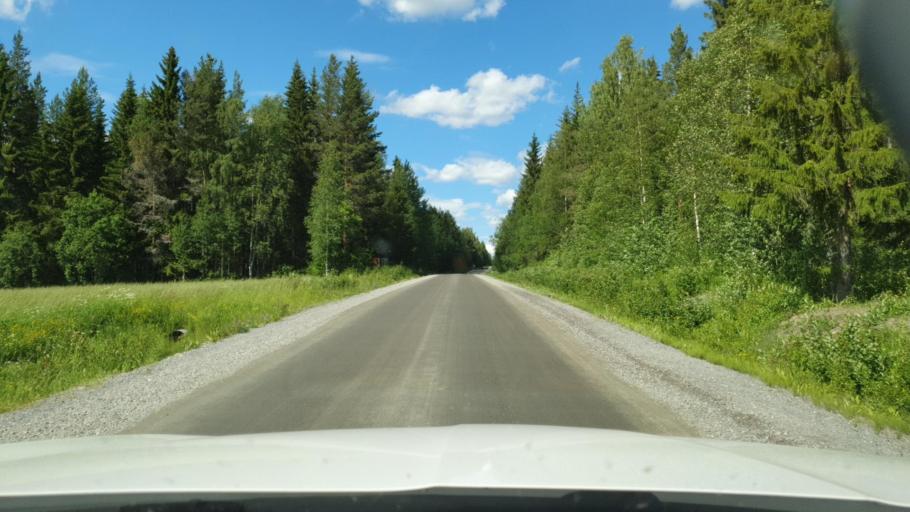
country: SE
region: Vaesterbotten
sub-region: Skelleftea Kommun
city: Forsbacka
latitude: 64.7926
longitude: 20.5080
